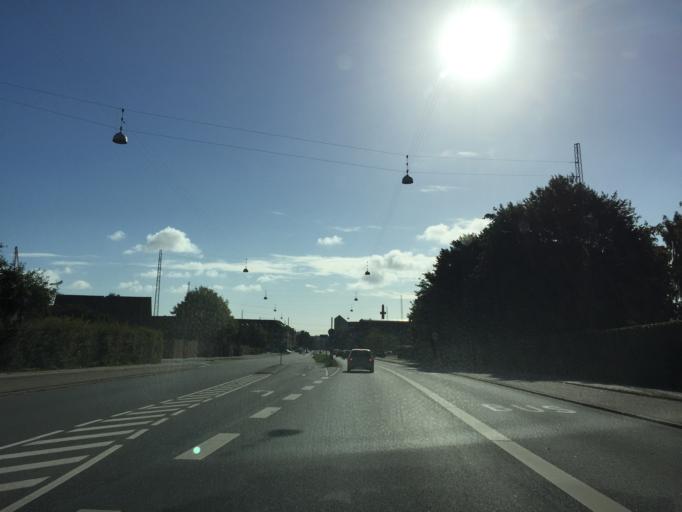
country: DK
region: Central Jutland
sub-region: Arhus Kommune
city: Arhus
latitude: 56.1620
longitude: 10.1796
